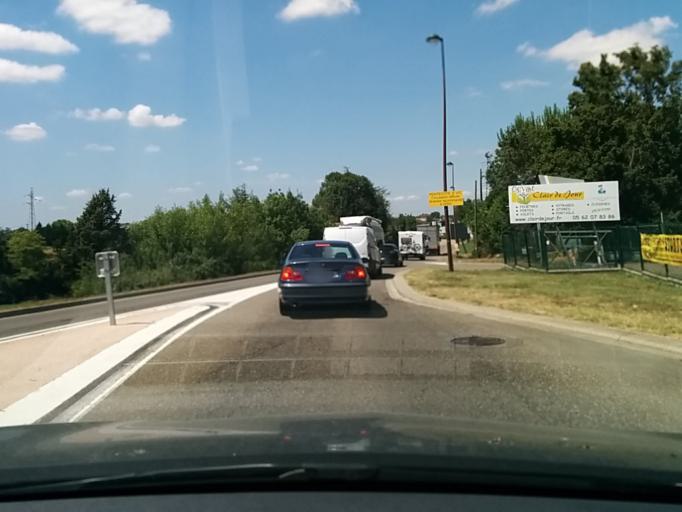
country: FR
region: Midi-Pyrenees
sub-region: Departement du Gers
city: Vic-Fezensac
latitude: 43.7524
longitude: 0.3132
